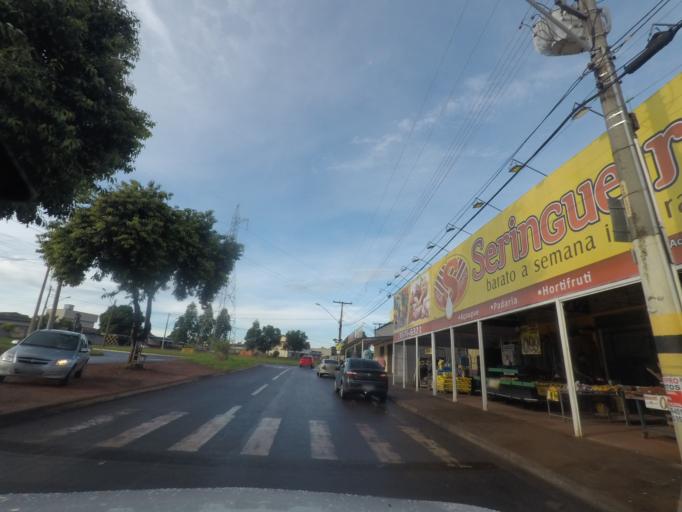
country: BR
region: Goias
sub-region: Goiania
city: Goiania
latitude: -16.7379
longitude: -49.3689
